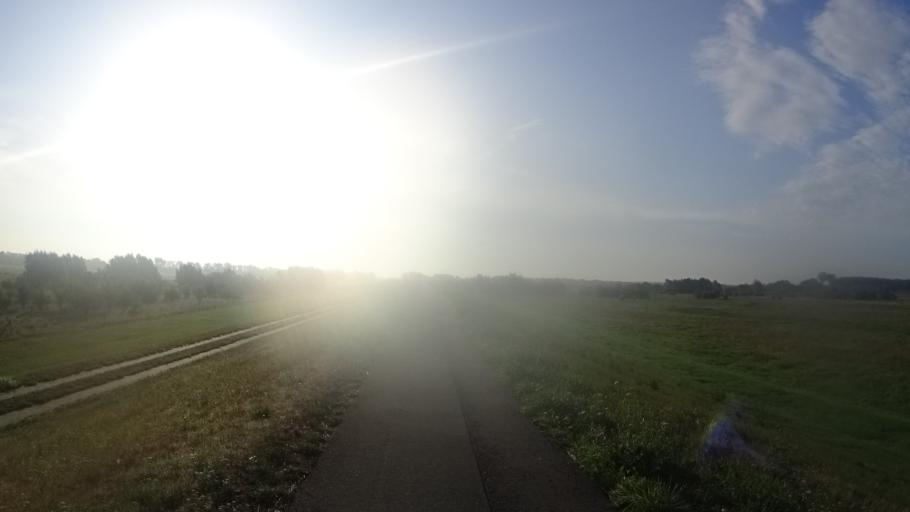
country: DE
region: Brandenburg
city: Lenzen
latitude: 53.0644
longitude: 11.5023
